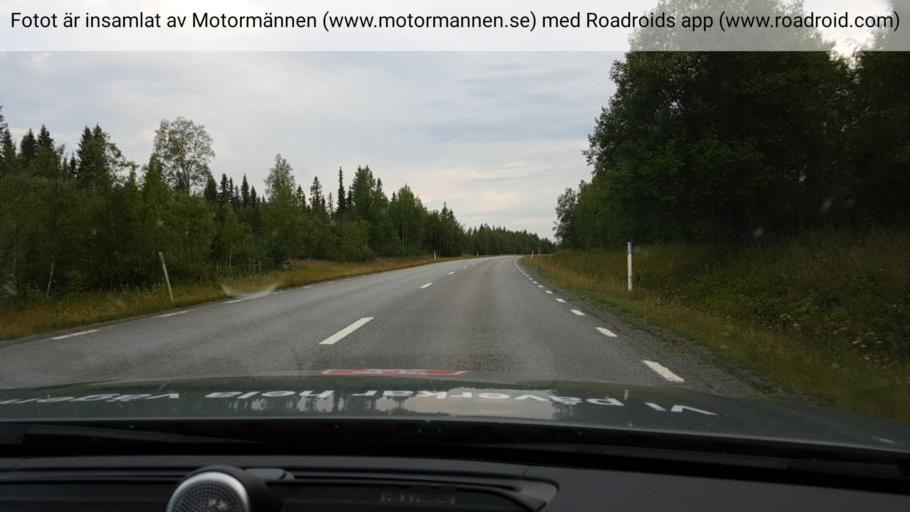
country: SE
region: Jaemtland
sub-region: OEstersunds Kommun
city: Lit
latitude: 63.4614
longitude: 15.1820
